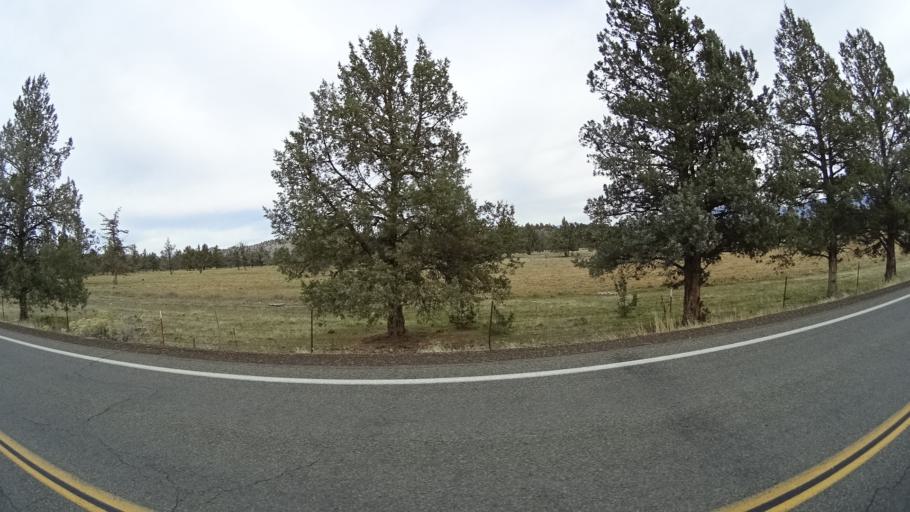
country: US
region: California
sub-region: Siskiyou County
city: Montague
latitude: 41.6342
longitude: -122.4374
